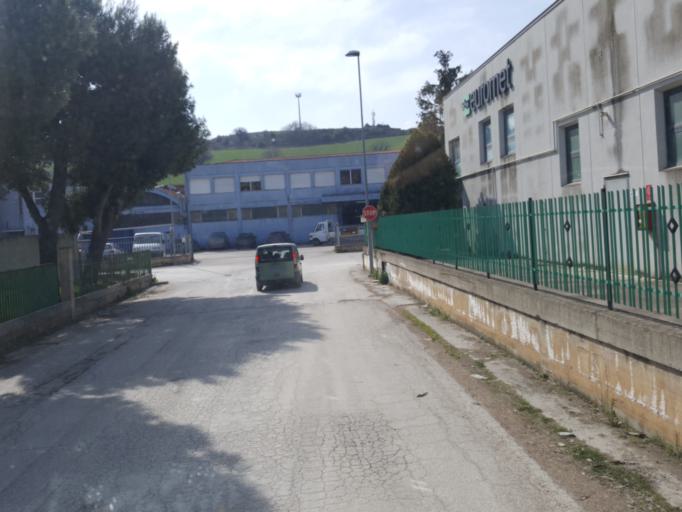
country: IT
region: The Marches
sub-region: Provincia di Ancona
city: Loreto Stazione
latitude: 43.4396
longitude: 13.6302
